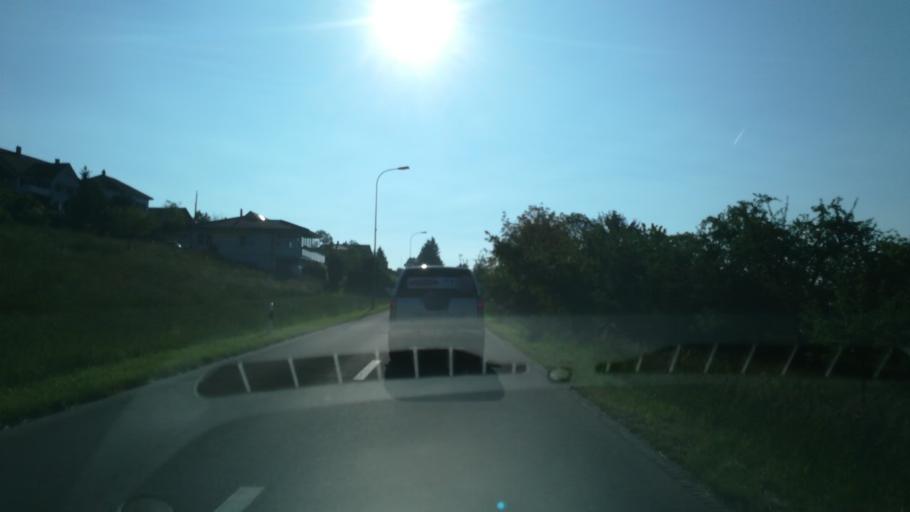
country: CH
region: Thurgau
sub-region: Frauenfeld District
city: Homburg
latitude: 47.6343
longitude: 9.0083
